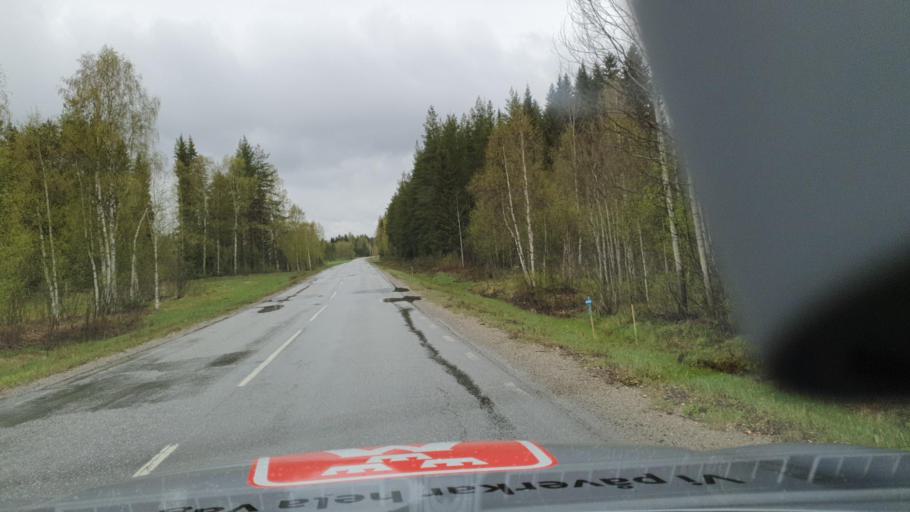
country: SE
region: Vaesternorrland
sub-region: OErnskoeldsviks Kommun
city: Bredbyn
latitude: 63.4927
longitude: 17.8568
